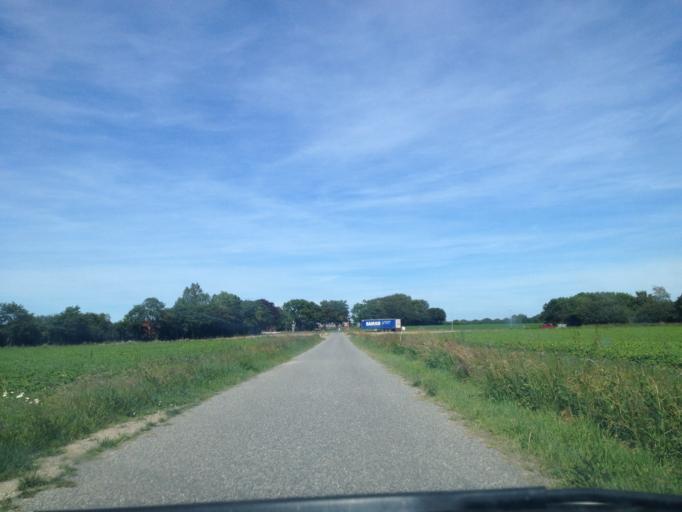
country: DK
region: Central Jutland
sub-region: Samso Kommune
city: Tranebjerg
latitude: 55.9564
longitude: 10.5526
